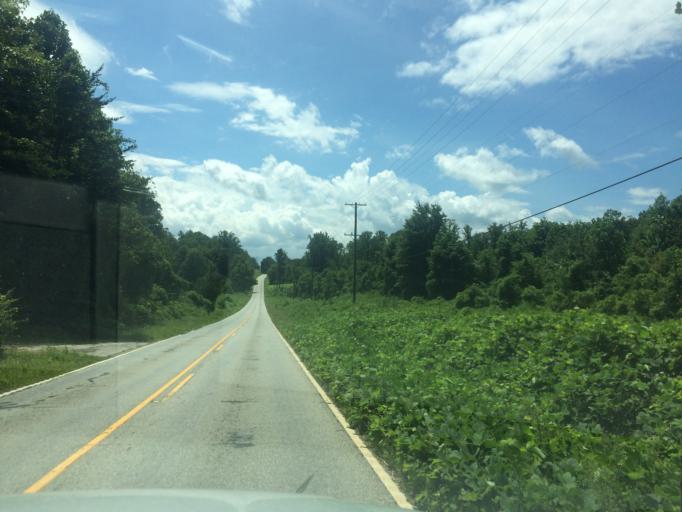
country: US
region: North Carolina
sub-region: Rutherford County
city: Lake Lure
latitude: 35.3896
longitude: -82.1929
